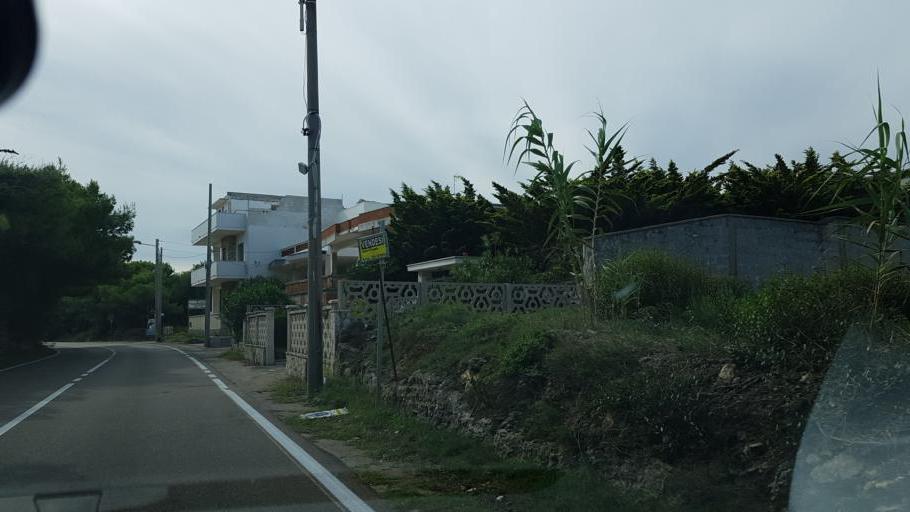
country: IT
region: Apulia
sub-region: Provincia di Lecce
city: Melendugno
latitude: 40.3239
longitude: 18.3765
